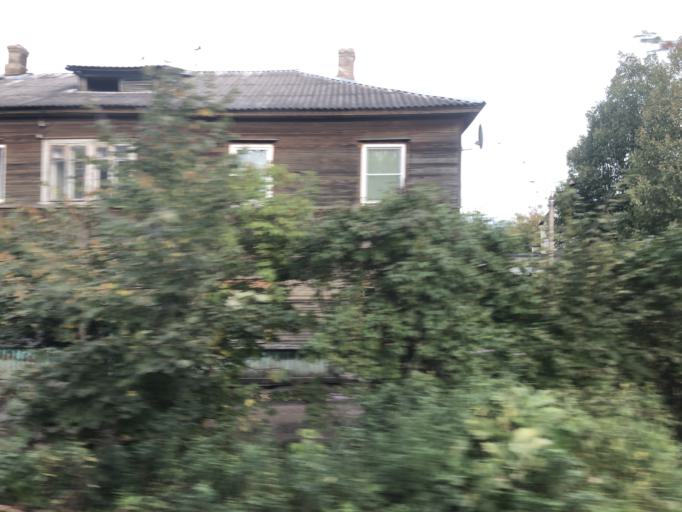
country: RU
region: Tverskaya
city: Rzhev
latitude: 56.2529
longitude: 34.2930
